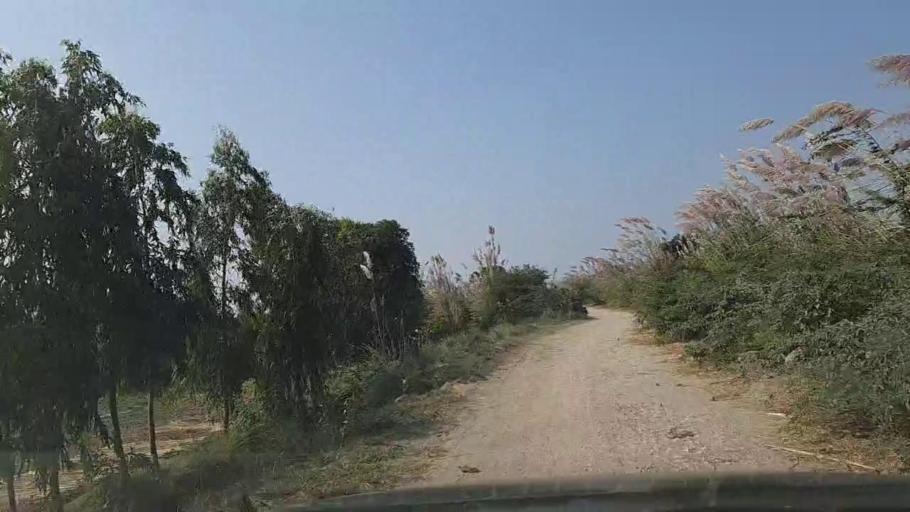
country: PK
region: Sindh
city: Gharo
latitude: 24.7017
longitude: 67.6310
